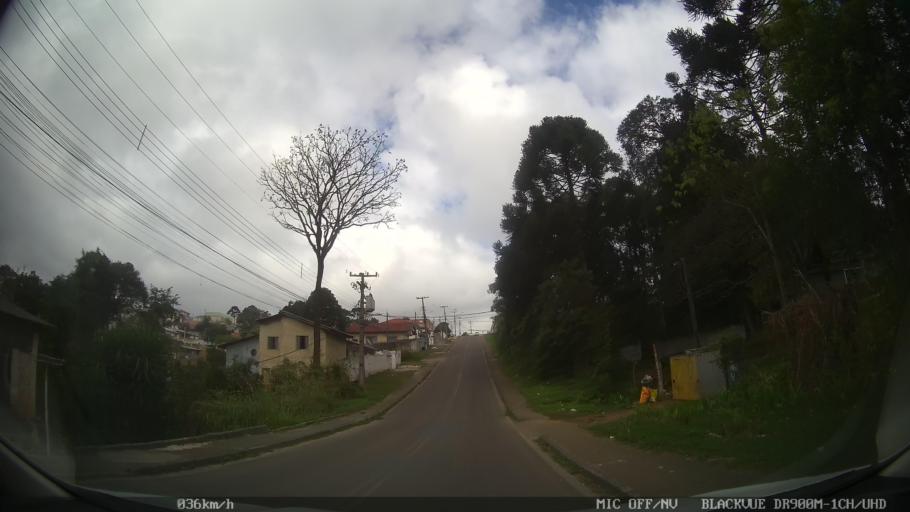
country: BR
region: Parana
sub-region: Colombo
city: Colombo
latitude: -25.3442
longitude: -49.2414
